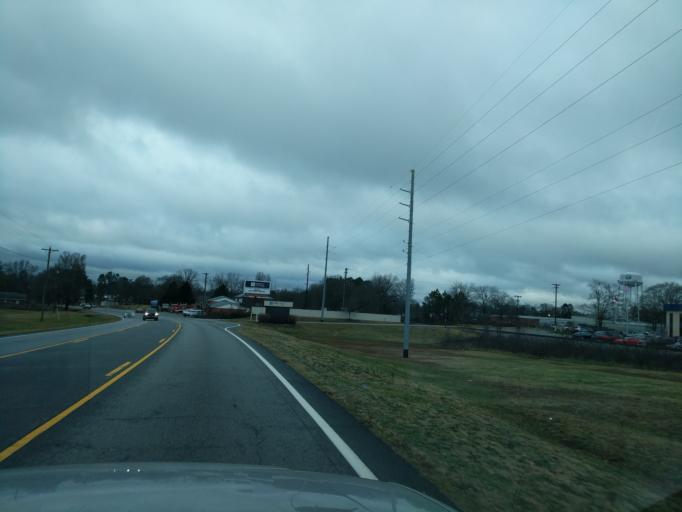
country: US
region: Georgia
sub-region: Franklin County
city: Lavonia
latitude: 34.4135
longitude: -83.0986
